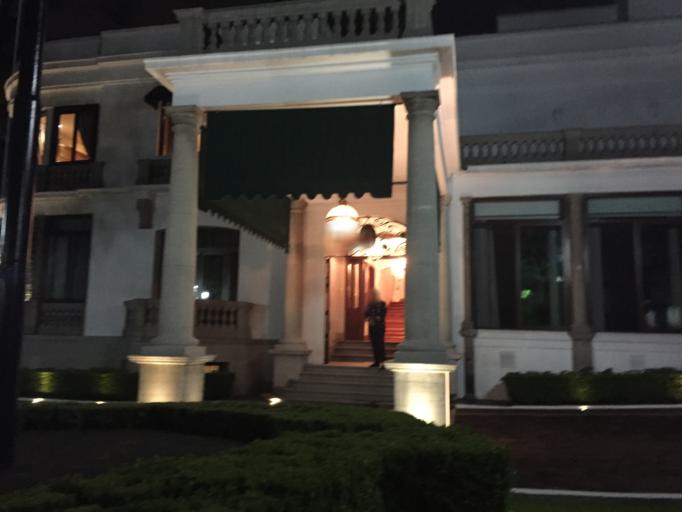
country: MX
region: Mexico City
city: Polanco
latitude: 19.4140
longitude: -99.1915
